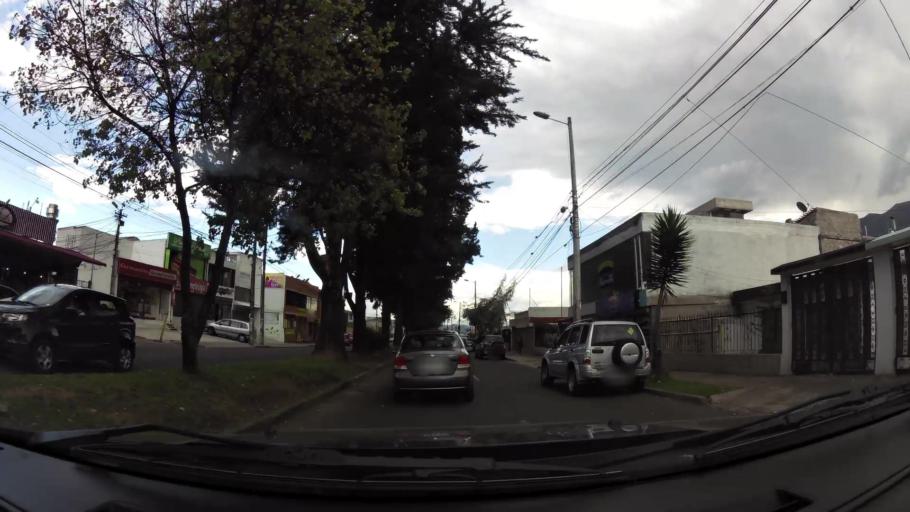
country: EC
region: Pichincha
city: Quito
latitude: -0.1345
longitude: -78.4867
